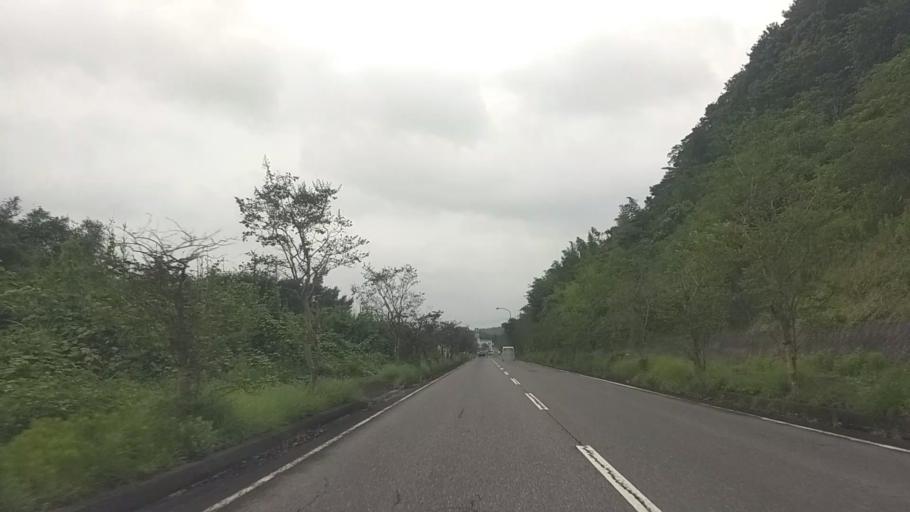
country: JP
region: Chiba
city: Kisarazu
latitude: 35.3785
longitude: 140.0091
